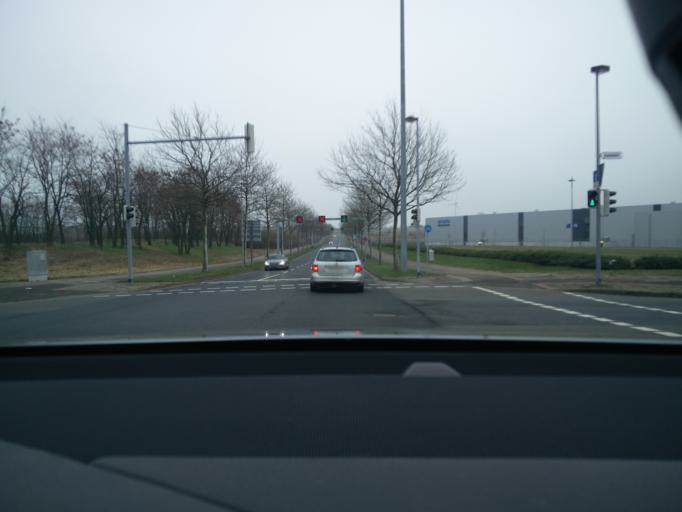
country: DE
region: Lower Saxony
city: Laatzen
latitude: 52.3314
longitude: 9.8194
